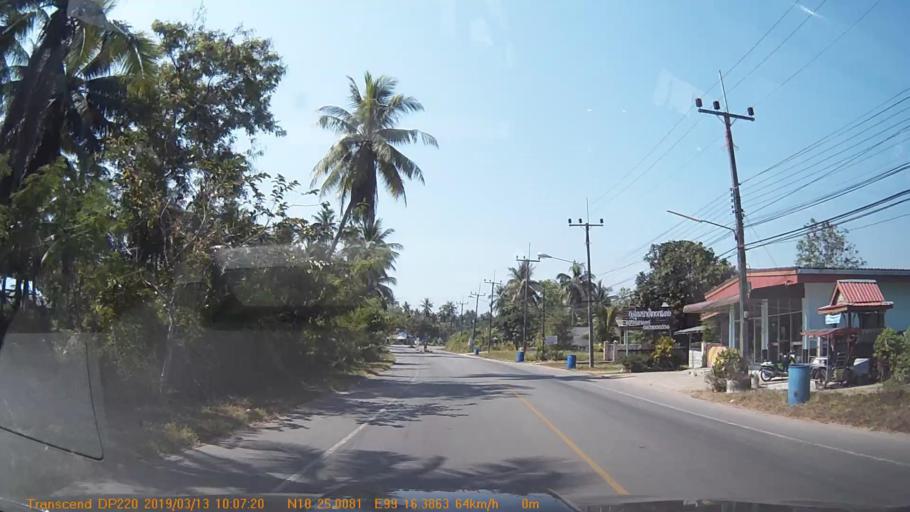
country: TH
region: Chumphon
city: Chumphon
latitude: 10.4167
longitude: 99.2730
